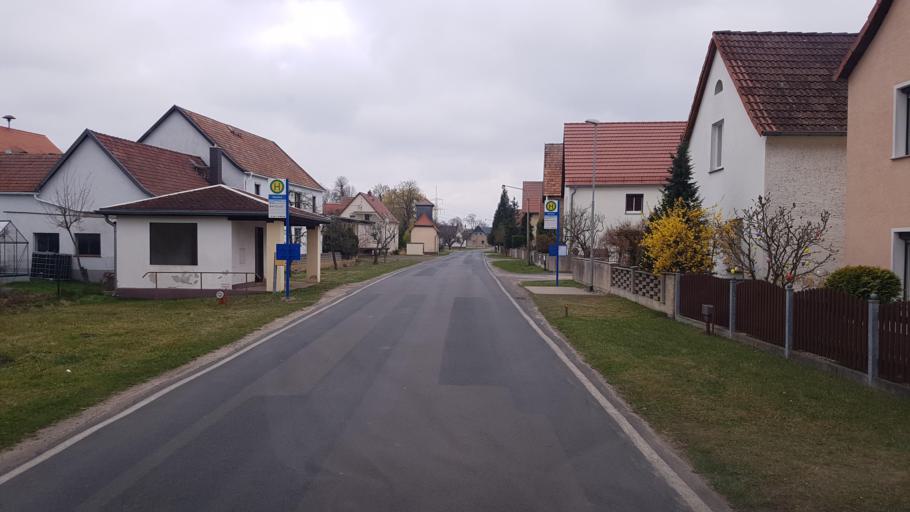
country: DE
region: Saxony
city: Nauwalde
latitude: 51.4204
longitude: 13.3899
